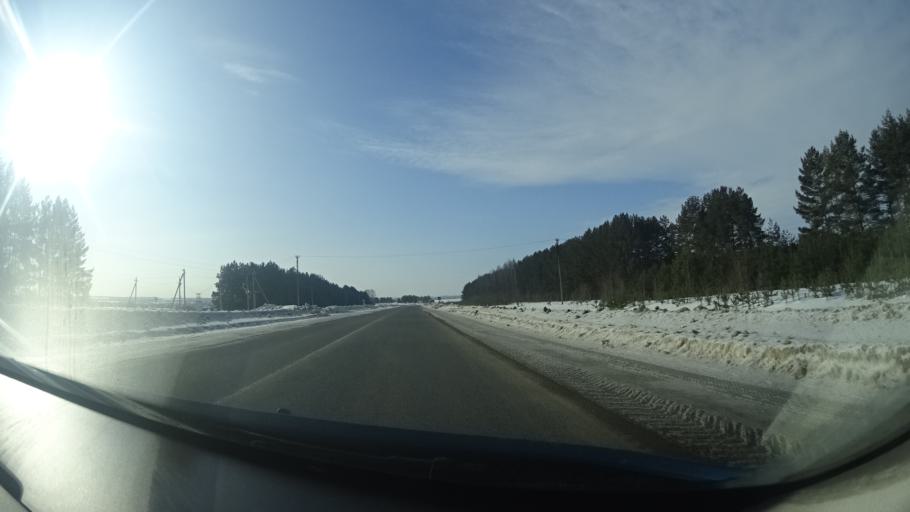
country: RU
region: Perm
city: Kuyeda
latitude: 56.4775
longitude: 55.5903
